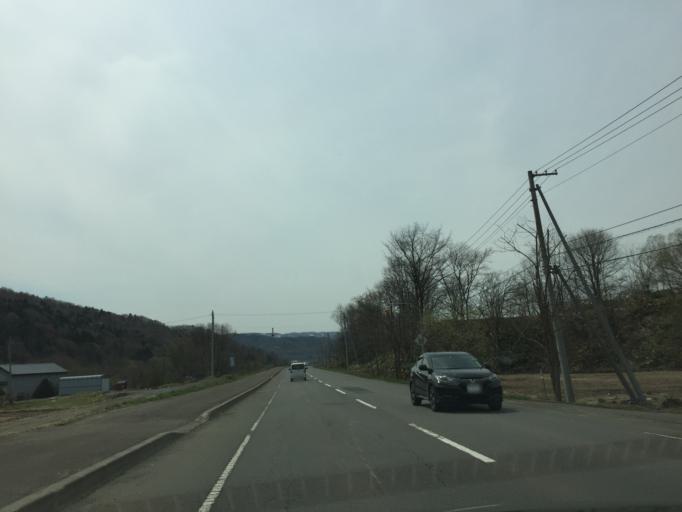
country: JP
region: Hokkaido
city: Ashibetsu
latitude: 43.5509
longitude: 142.1763
